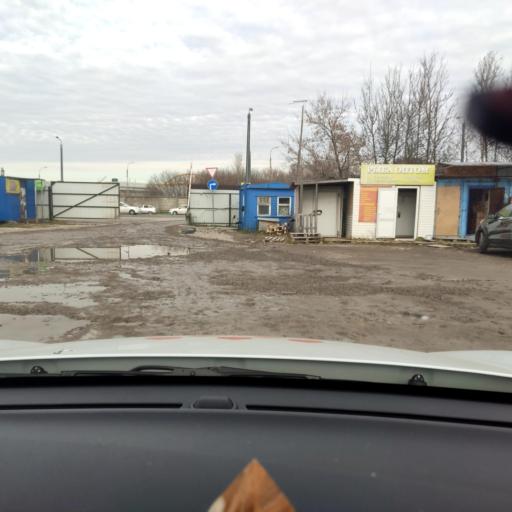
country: RU
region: Tatarstan
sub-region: Gorod Kazan'
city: Kazan
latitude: 55.8512
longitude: 49.1285
